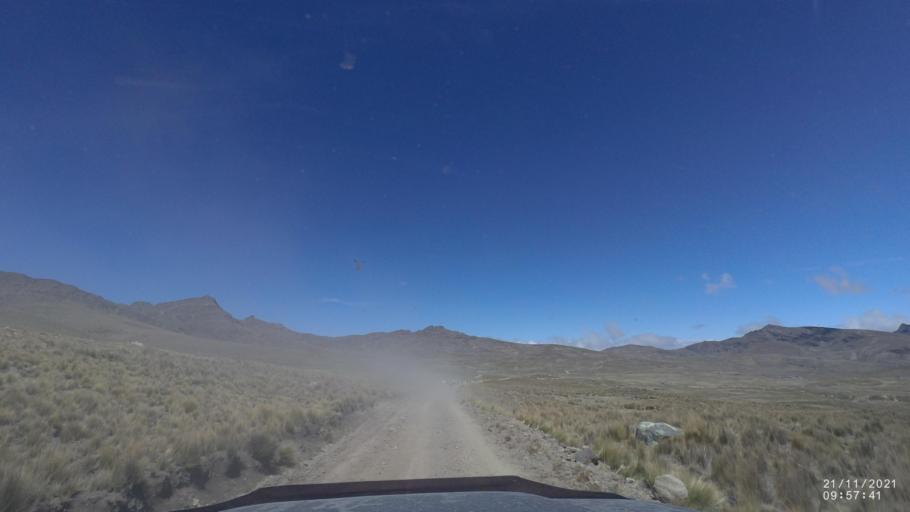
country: BO
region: Cochabamba
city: Cochabamba
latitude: -17.0383
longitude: -66.2725
